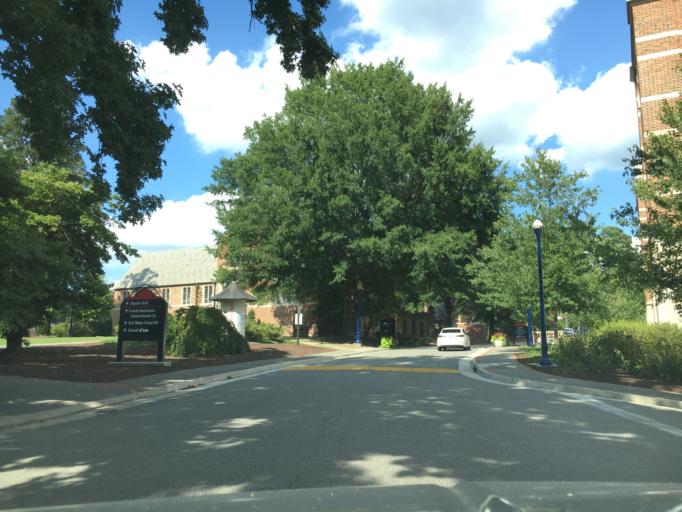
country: US
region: Virginia
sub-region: Henrico County
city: Tuckahoe
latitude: 37.5793
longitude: -77.5376
